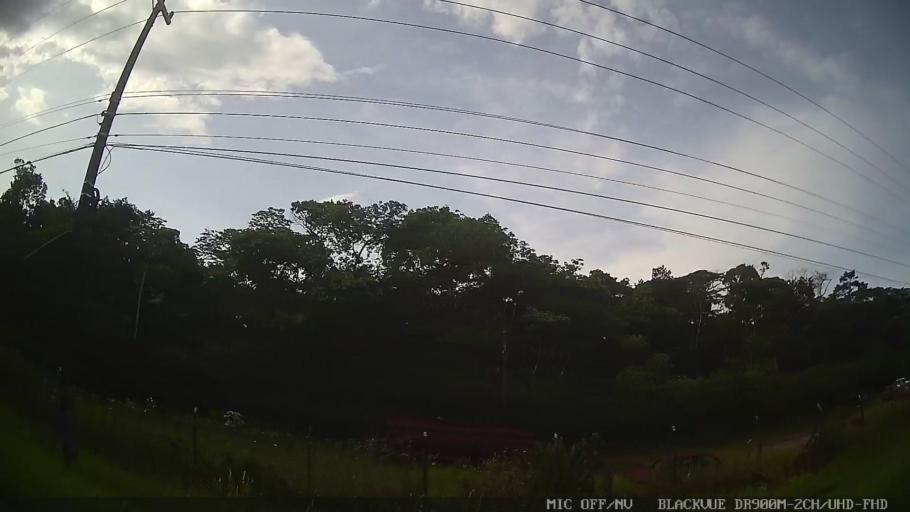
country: BR
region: Sao Paulo
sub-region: Bertioga
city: Bertioga
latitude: -23.7956
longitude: -46.0587
